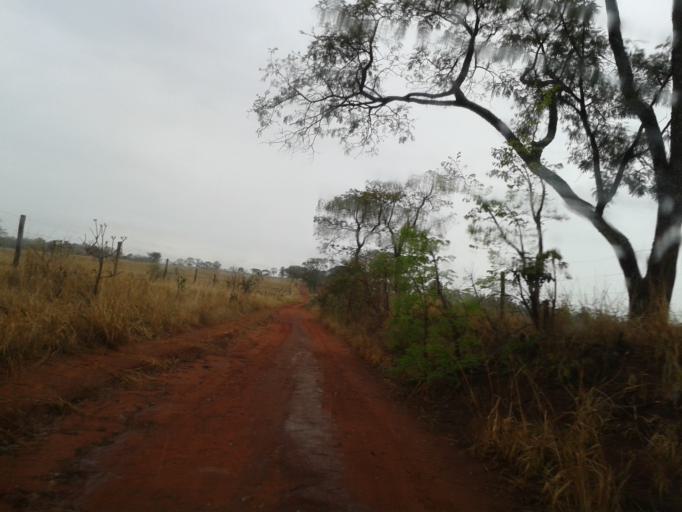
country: BR
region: Minas Gerais
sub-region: Campina Verde
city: Campina Verde
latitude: -19.3531
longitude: -49.5459
